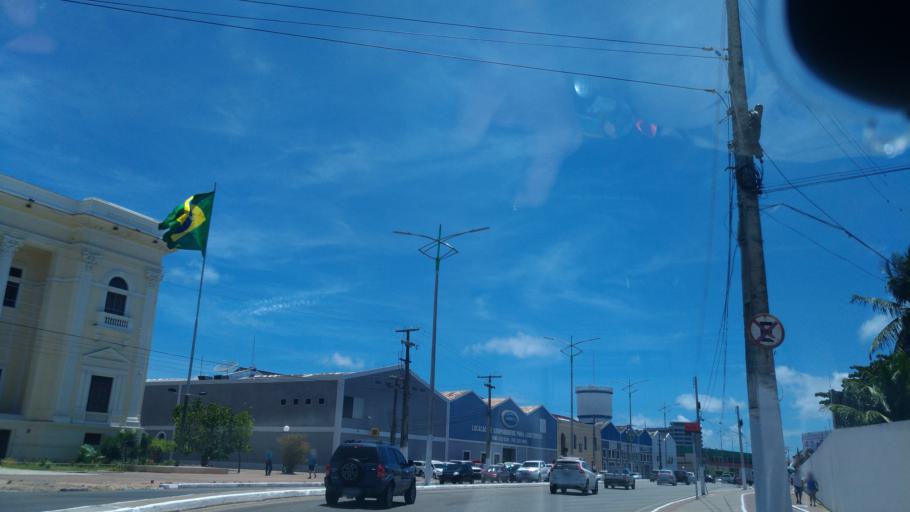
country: BR
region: Alagoas
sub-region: Maceio
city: Maceio
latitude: -9.6725
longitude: -35.7242
